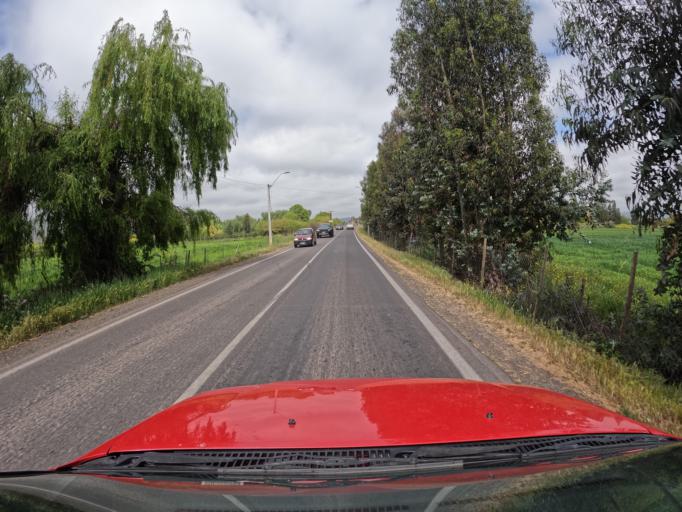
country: CL
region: O'Higgins
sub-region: Provincia de Colchagua
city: Santa Cruz
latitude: -34.6755
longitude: -71.3534
